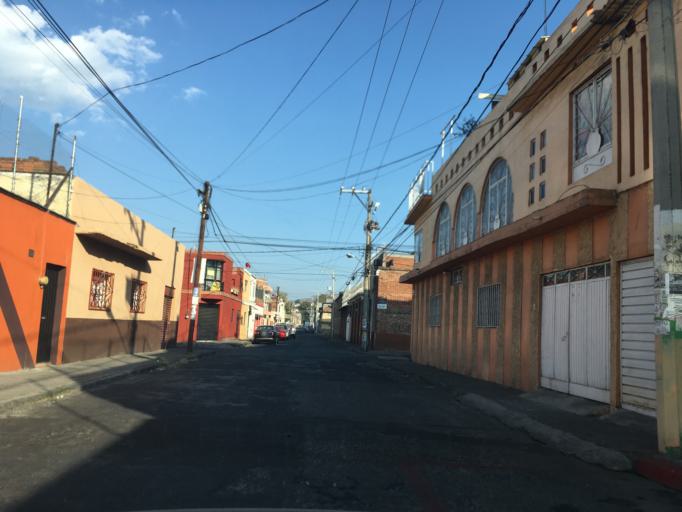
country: MX
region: Michoacan
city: Morelia
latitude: 19.7090
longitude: -101.1962
